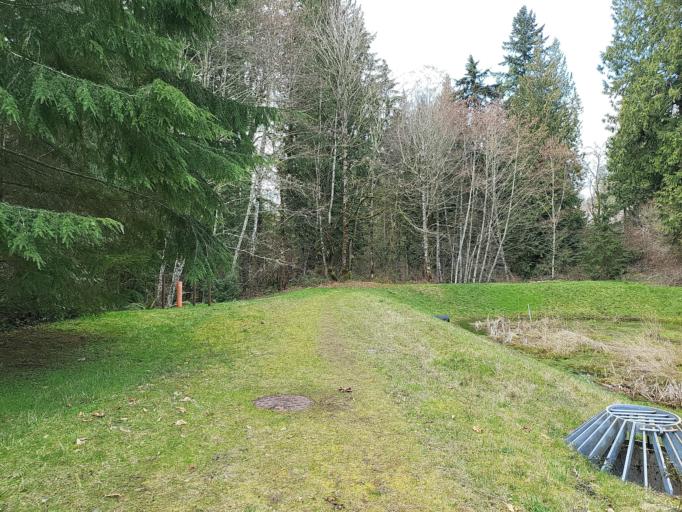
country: US
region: Washington
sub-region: King County
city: East Renton Highlands
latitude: 47.5130
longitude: -122.1192
